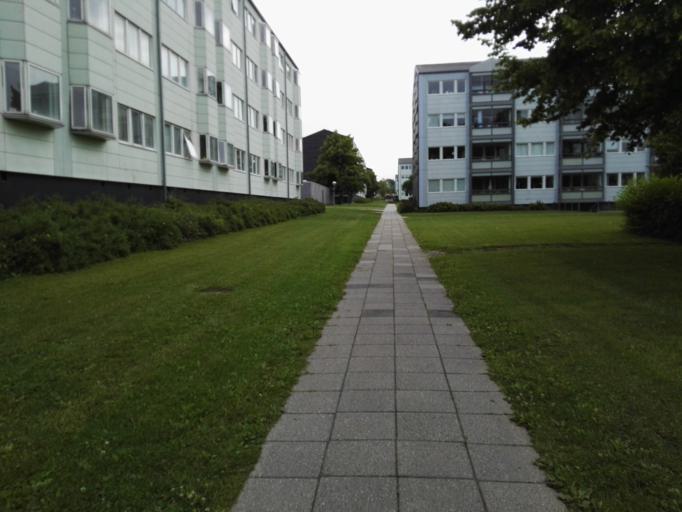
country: DK
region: Capital Region
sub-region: Ballerup Kommune
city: Ballerup
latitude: 55.7168
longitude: 12.3603
